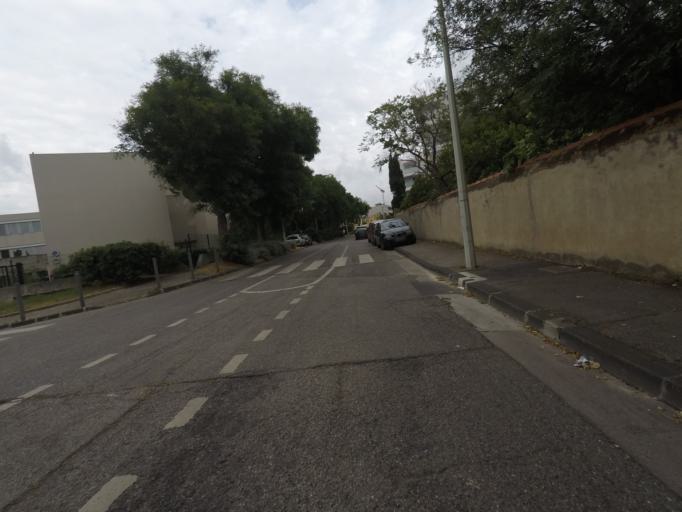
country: FR
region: Provence-Alpes-Cote d'Azur
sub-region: Departement des Bouches-du-Rhone
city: Marseille 08
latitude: 43.2517
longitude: 5.3848
